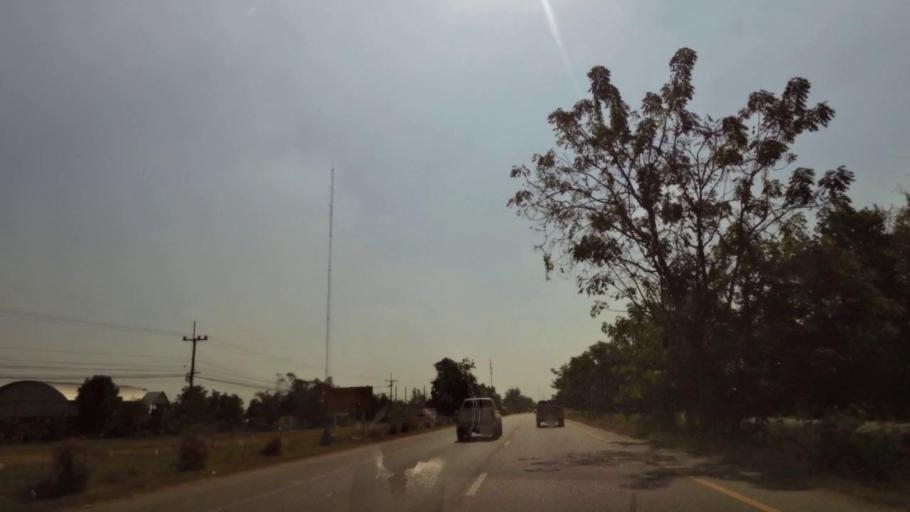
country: TH
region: Phichit
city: Wachira Barami
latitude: 16.4178
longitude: 100.1438
